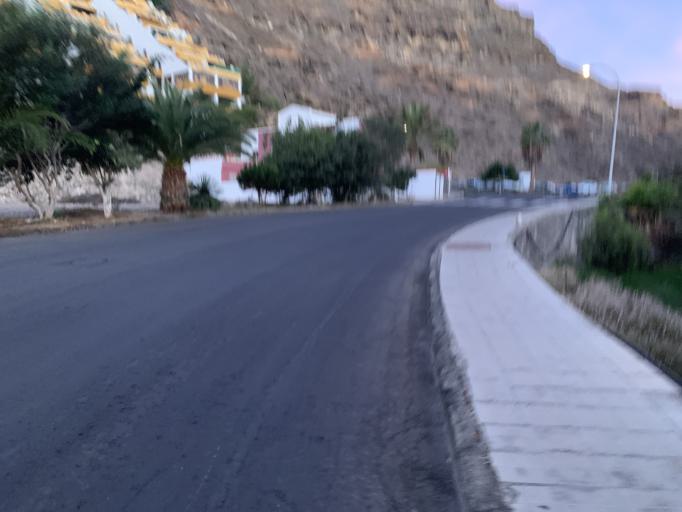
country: ES
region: Canary Islands
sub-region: Provincia de Las Palmas
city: Puerto Rico
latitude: 27.8032
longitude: -15.7321
